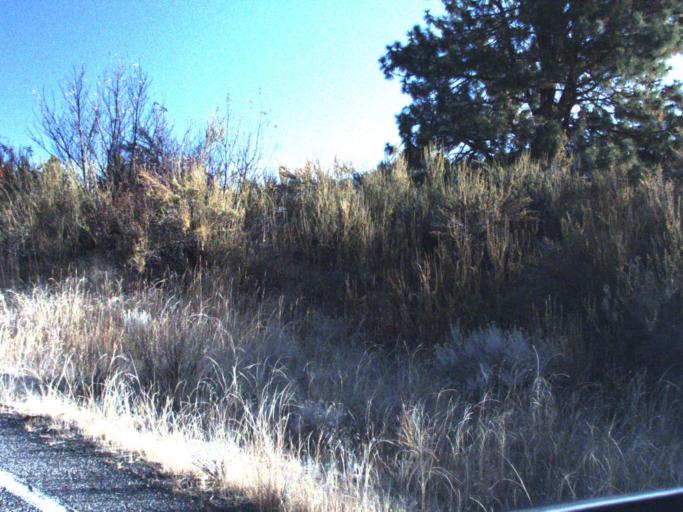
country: US
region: Washington
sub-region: Okanogan County
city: Coulee Dam
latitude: 47.9804
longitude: -118.6957
